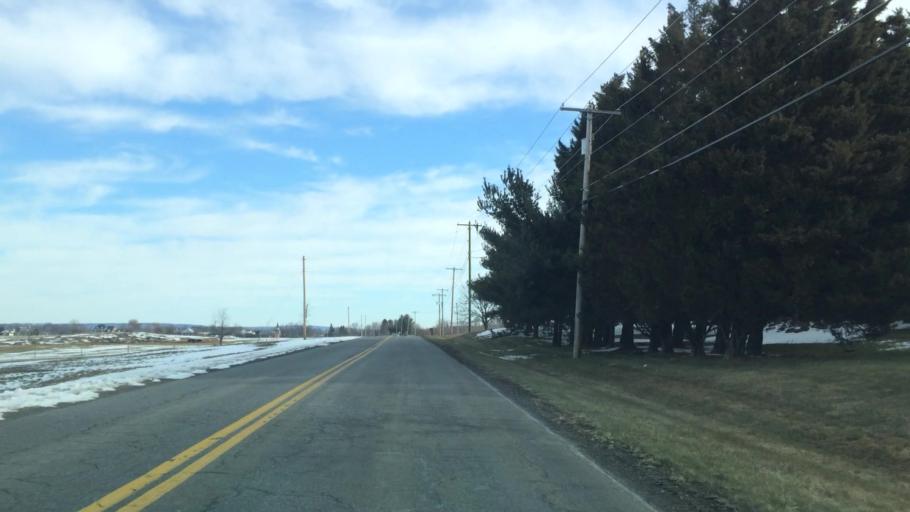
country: US
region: Virginia
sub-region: City of Winchester
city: Winchester
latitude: 39.2572
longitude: -78.1337
